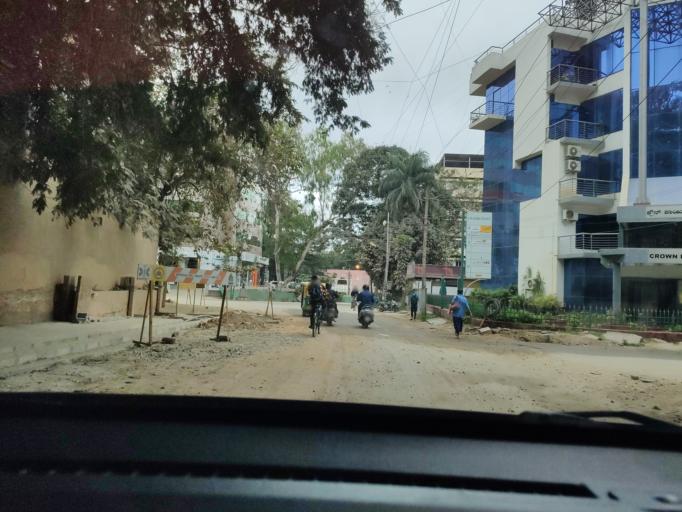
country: IN
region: Karnataka
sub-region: Bangalore Urban
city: Bangalore
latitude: 12.9737
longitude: 77.5994
